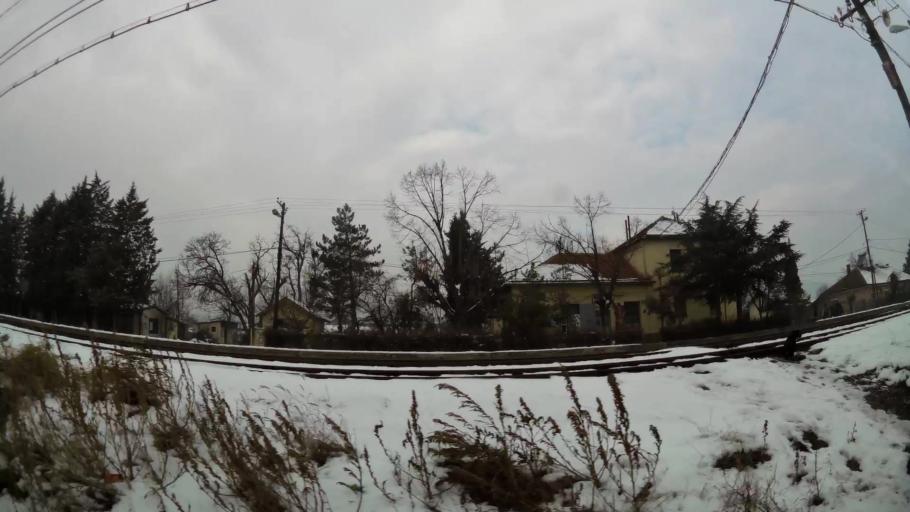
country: MK
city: Kondovo
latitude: 42.0469
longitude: 21.3541
